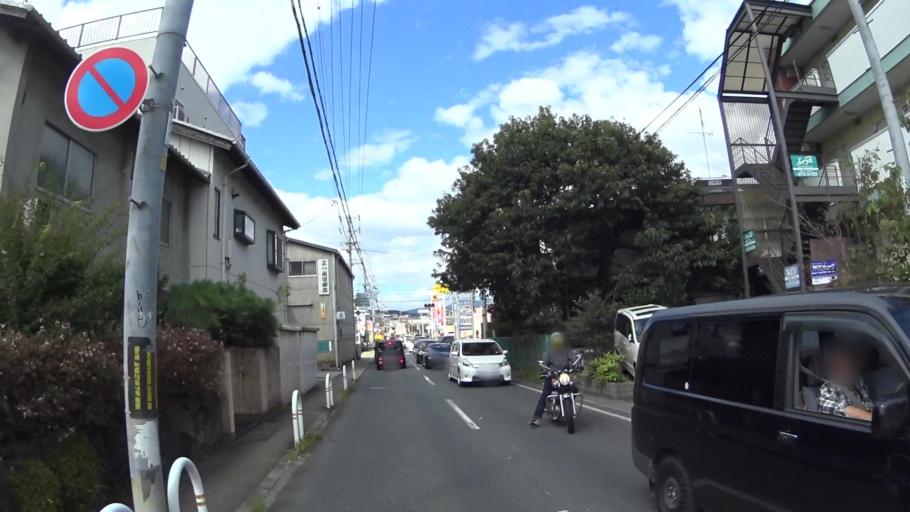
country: JP
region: Kyoto
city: Uji
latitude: 34.9281
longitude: 135.7997
